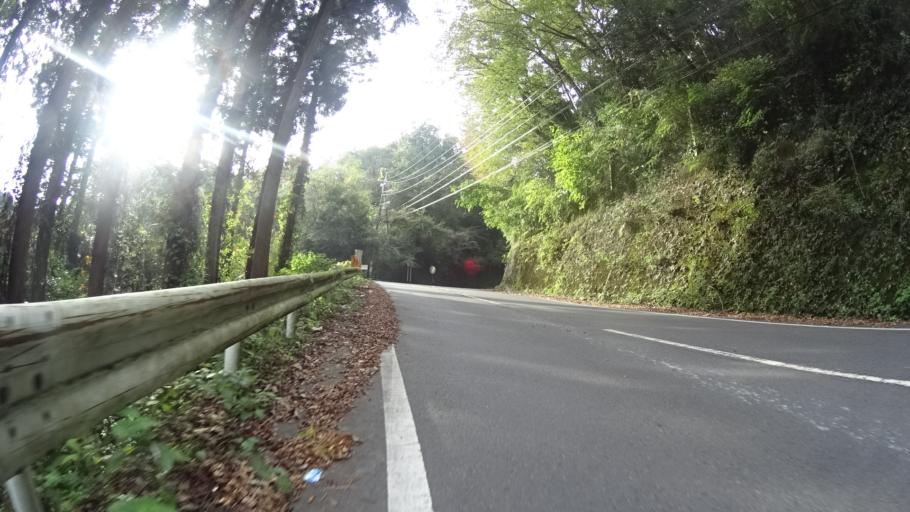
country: JP
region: Yamanashi
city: Uenohara
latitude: 35.6391
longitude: 139.0760
